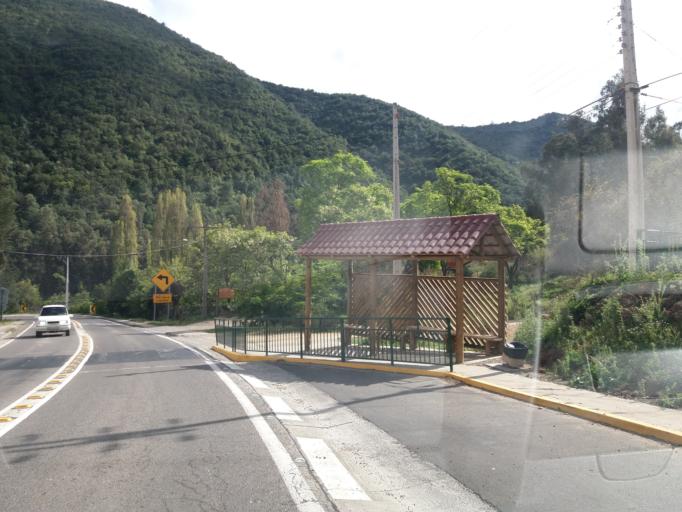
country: CL
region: Valparaiso
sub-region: Provincia de Marga Marga
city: Limache
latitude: -33.0639
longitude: -71.0656
